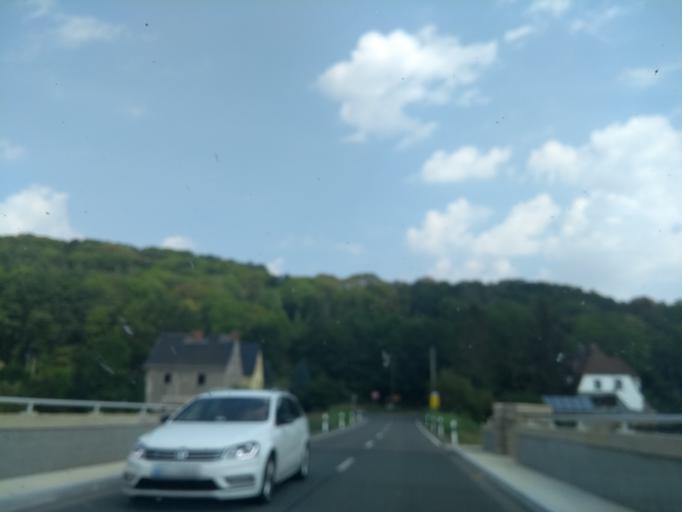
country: DE
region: Saxony-Anhalt
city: Kretzschau
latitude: 51.0263
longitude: 12.0635
